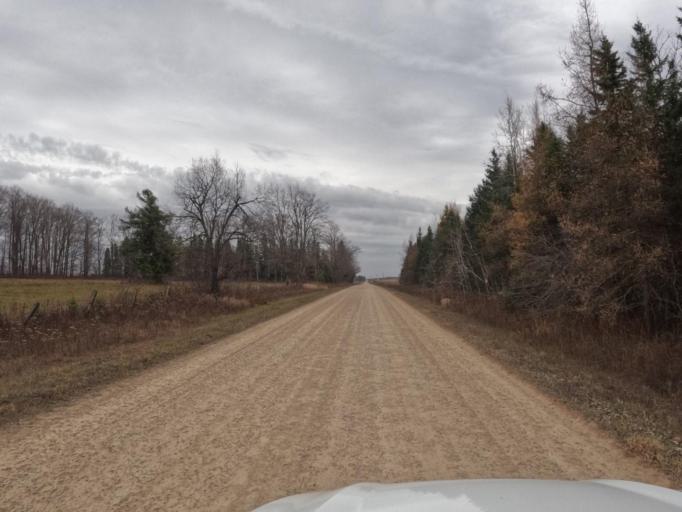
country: CA
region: Ontario
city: Shelburne
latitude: 44.0243
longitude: -80.3927
